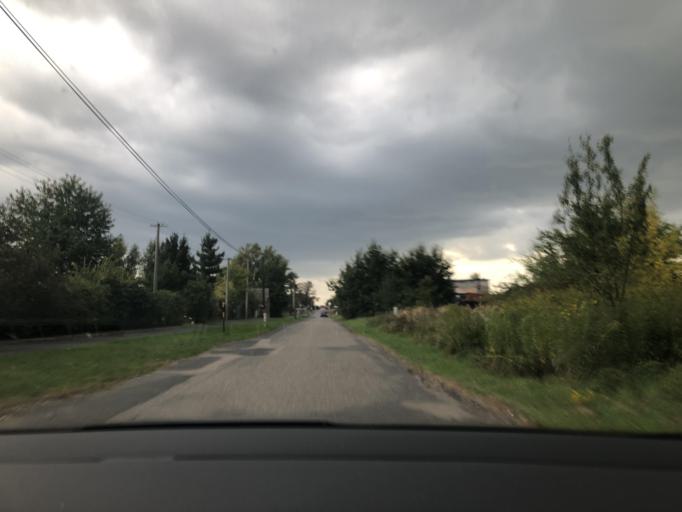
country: CZ
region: Central Bohemia
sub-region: Okres Kolin
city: Tynec nad Labem
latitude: 50.0488
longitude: 15.3670
